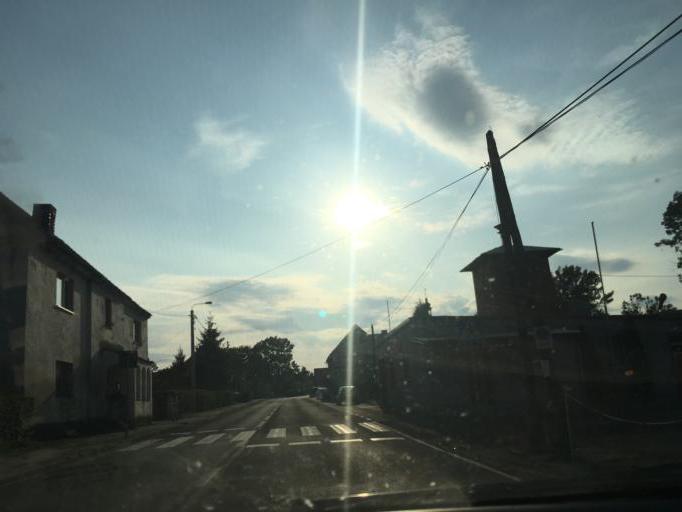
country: PL
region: Opole Voivodeship
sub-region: Powiat nyski
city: Kamienica
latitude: 50.4499
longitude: 16.9546
